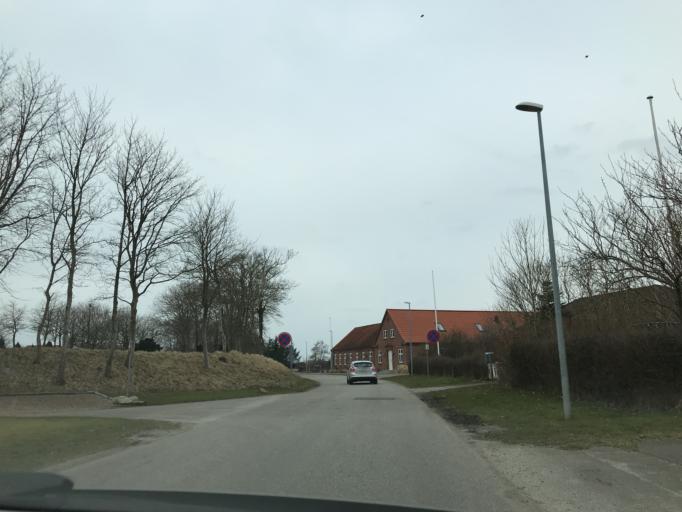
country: DK
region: South Denmark
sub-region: Varde Kommune
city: Oksbol
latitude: 55.8119
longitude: 8.2951
